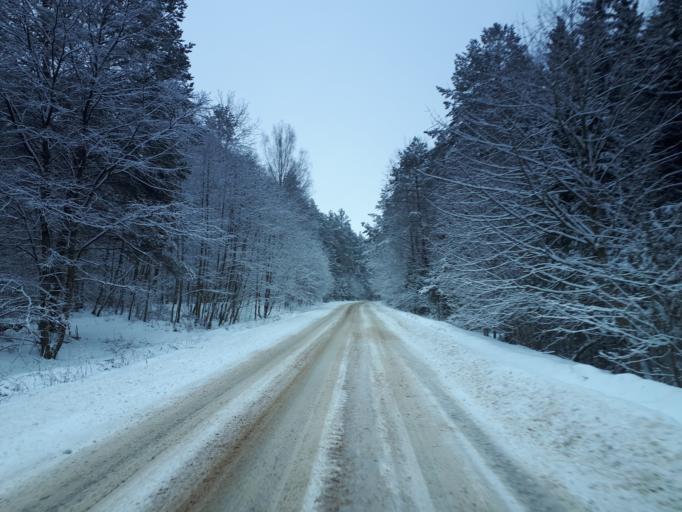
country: BY
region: Vitebsk
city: Vitebsk
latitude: 55.2643
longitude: 30.2154
